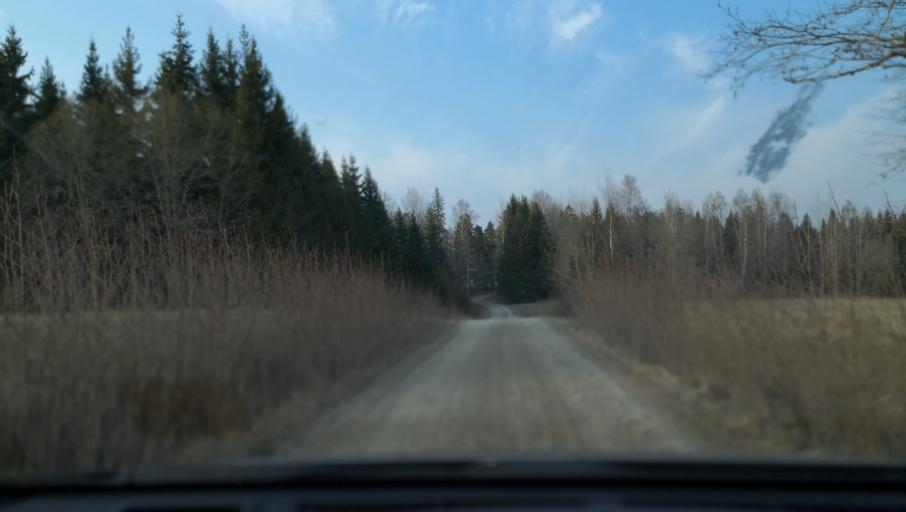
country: SE
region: OErebro
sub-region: Orebro Kommun
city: Hovsta
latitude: 59.3916
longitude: 15.2706
